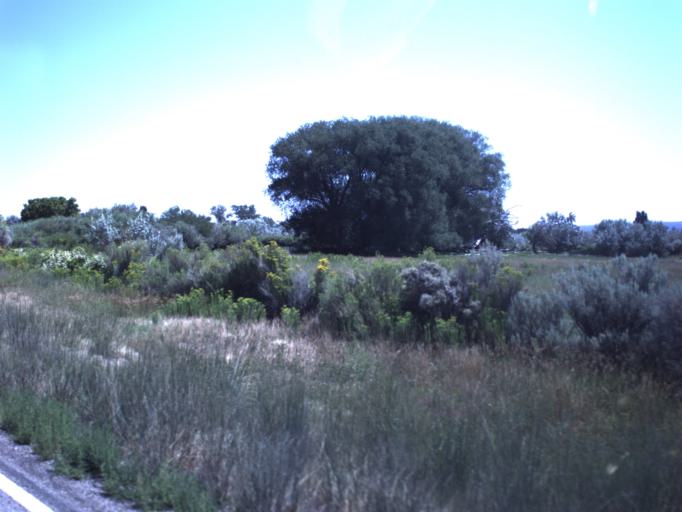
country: US
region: Utah
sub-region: Emery County
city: Ferron
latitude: 38.9022
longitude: -111.2735
